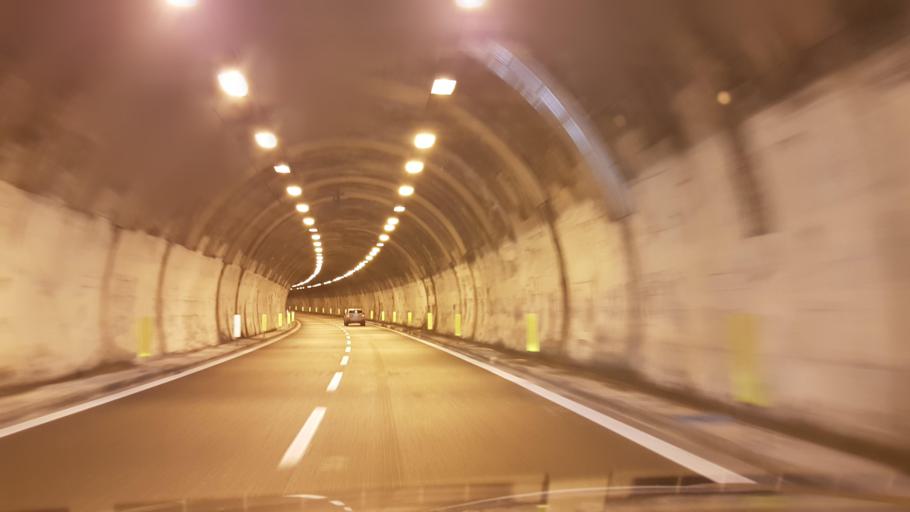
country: IT
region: Liguria
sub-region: Provincia di Imperia
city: Diano Castello
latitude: 43.9206
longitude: 8.0714
